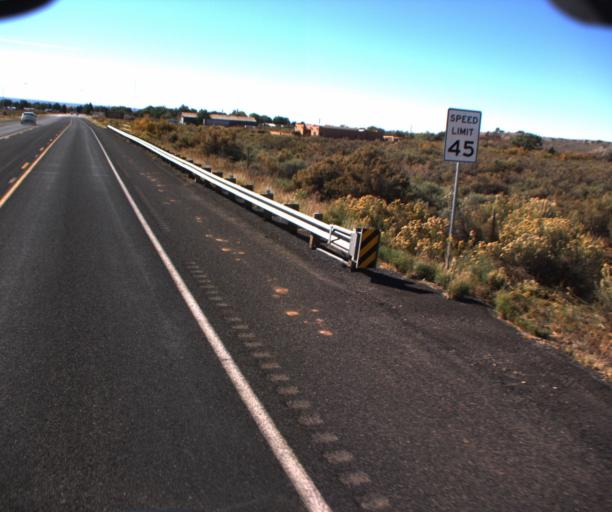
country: US
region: Arizona
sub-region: Coconino County
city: Fredonia
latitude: 36.9644
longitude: -112.5269
